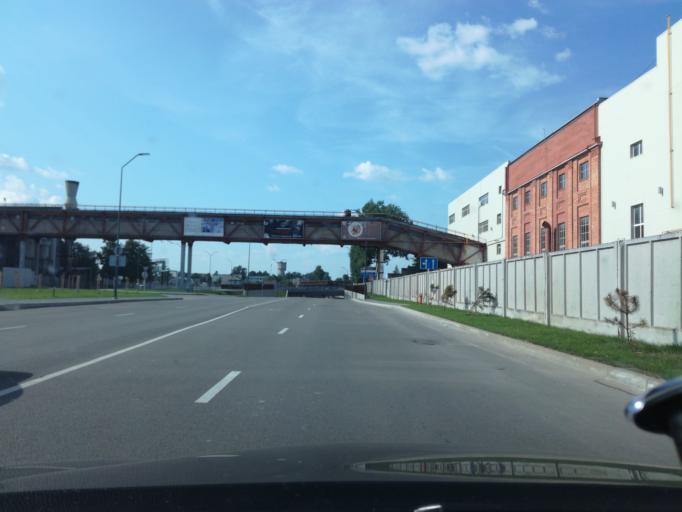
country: LT
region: Marijampoles apskritis
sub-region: Marijampole Municipality
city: Marijampole
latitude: 54.5360
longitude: 23.3519
